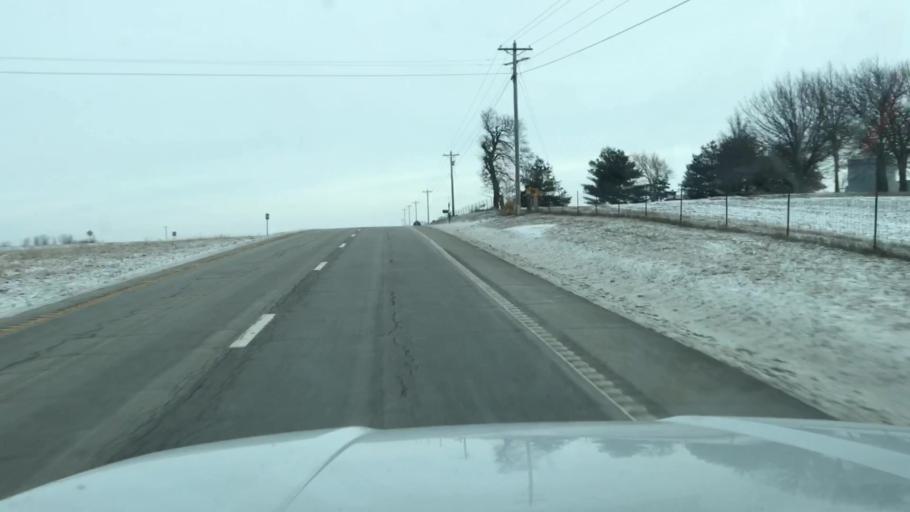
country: US
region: Missouri
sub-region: Andrew County
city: Savannah
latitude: 39.9920
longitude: -94.8799
